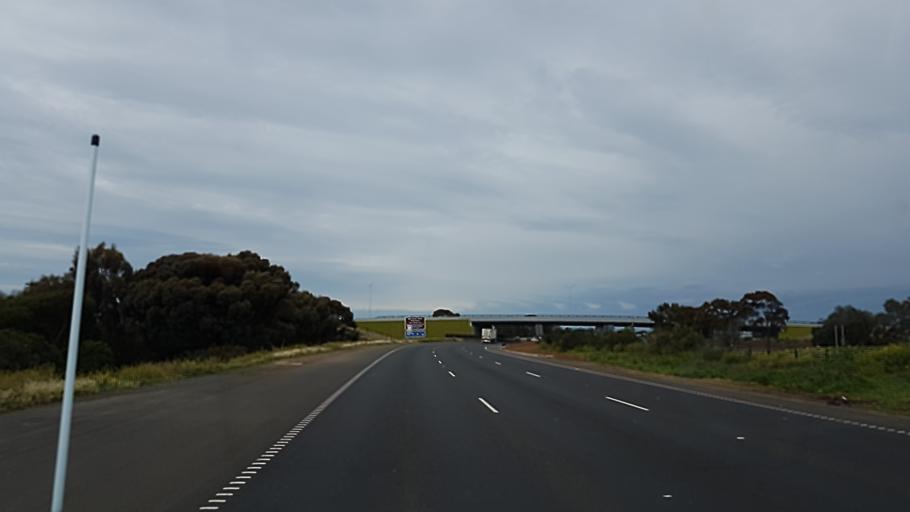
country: AU
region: Victoria
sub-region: Wyndham
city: Hoppers Crossing
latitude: -37.8962
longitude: 144.7084
